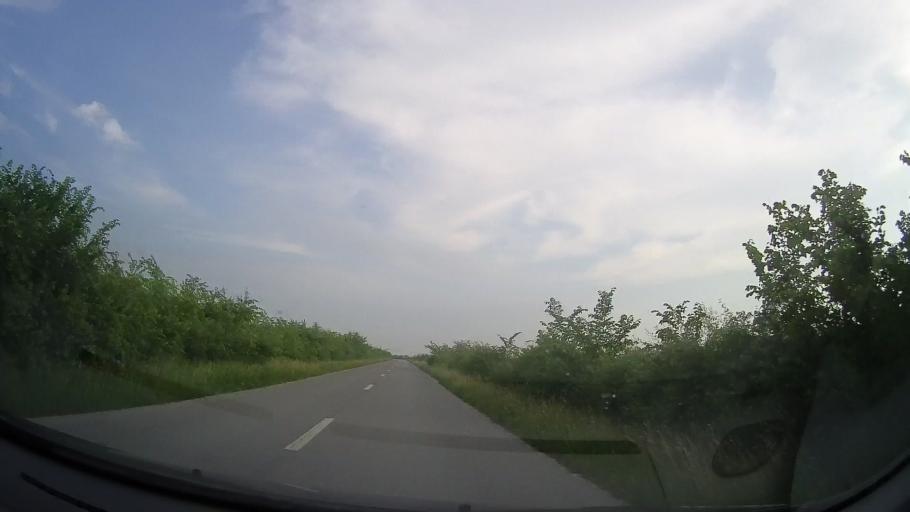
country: RO
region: Timis
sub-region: Comuna Foeni
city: Foeni
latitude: 45.4882
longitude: 20.8419
